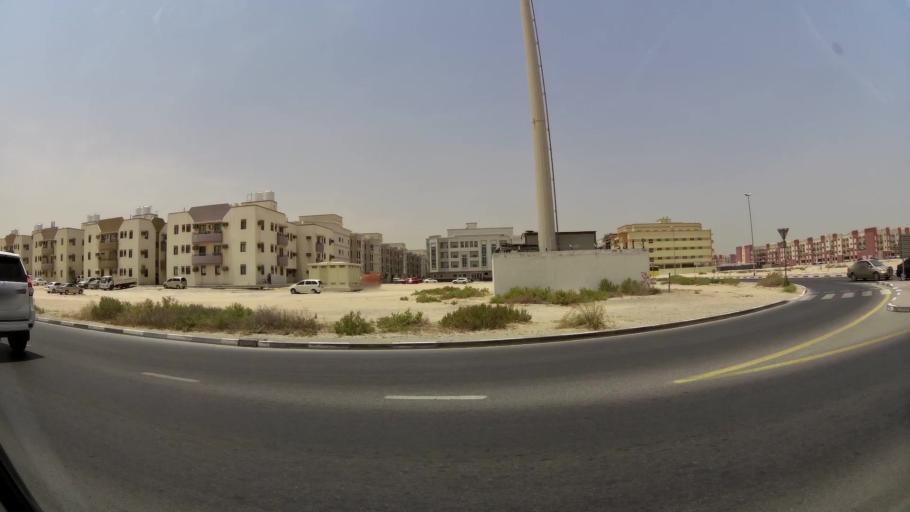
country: AE
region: Ash Shariqah
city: Sharjah
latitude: 25.2837
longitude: 55.4091
